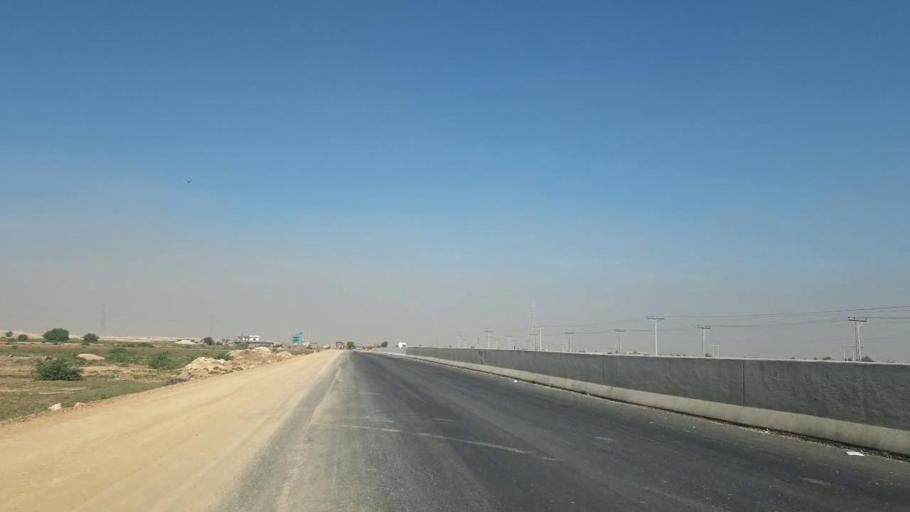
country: PK
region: Sindh
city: Jamshoro
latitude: 25.5181
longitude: 68.2741
